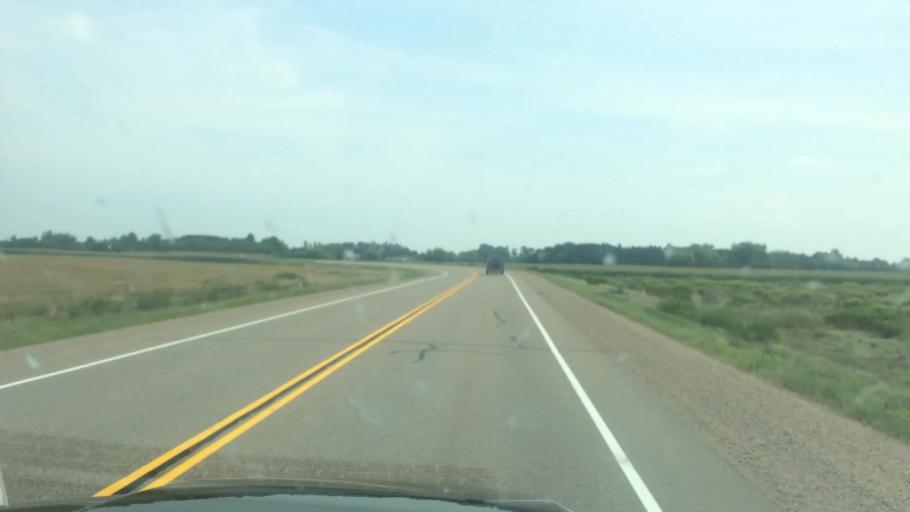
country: US
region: Wisconsin
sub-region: Langlade County
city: Antigo
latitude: 45.1421
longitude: -89.1879
